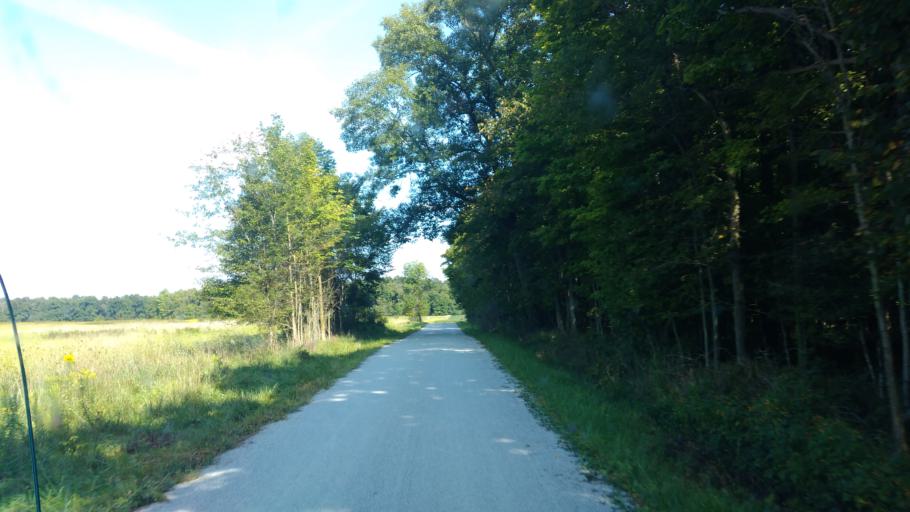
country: US
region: Ohio
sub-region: Hardin County
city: Kenton
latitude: 40.6294
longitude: -83.4414
